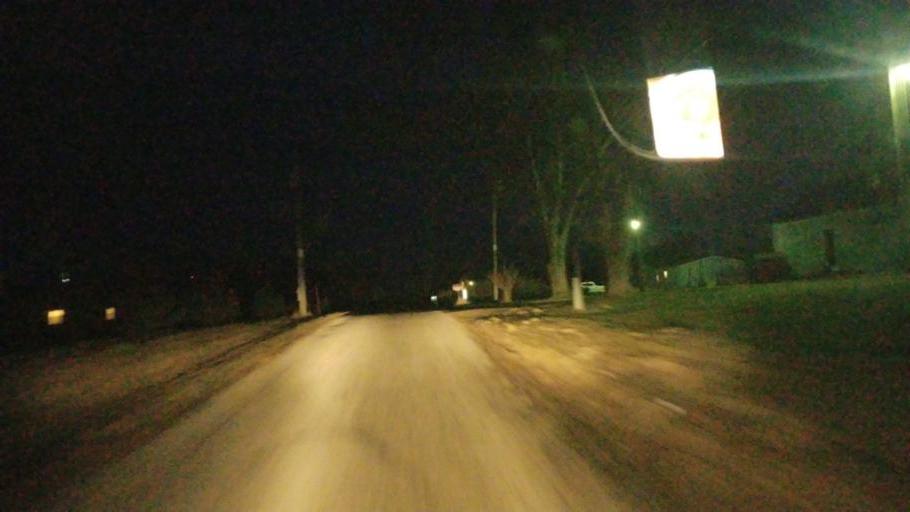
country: US
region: Ohio
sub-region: Defiance County
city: Hicksville
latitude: 41.3445
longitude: -84.7285
